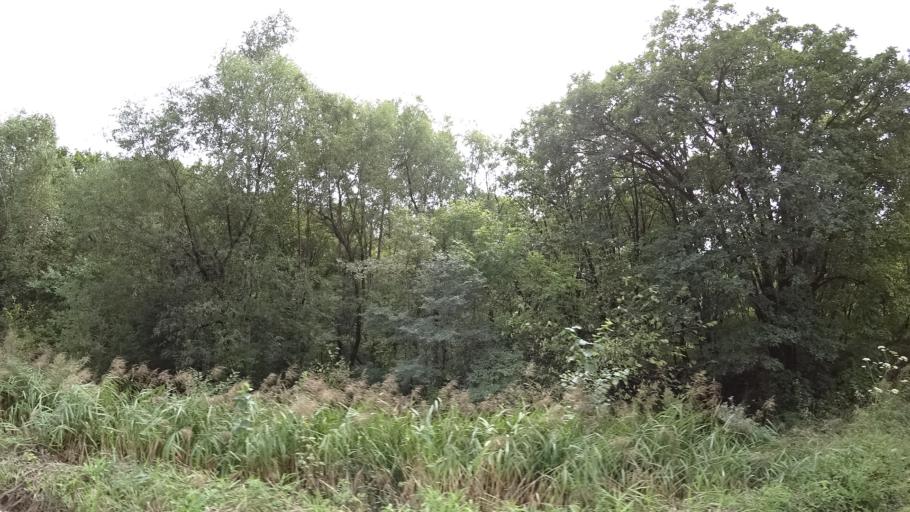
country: RU
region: Primorskiy
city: Lyalichi
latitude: 44.0994
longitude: 132.4260
